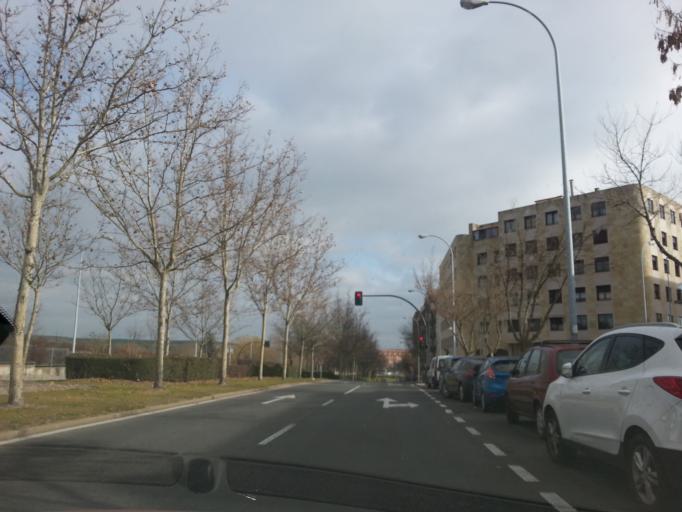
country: ES
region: Castille and Leon
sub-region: Provincia de Salamanca
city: Salamanca
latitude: 40.9795
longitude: -5.6556
